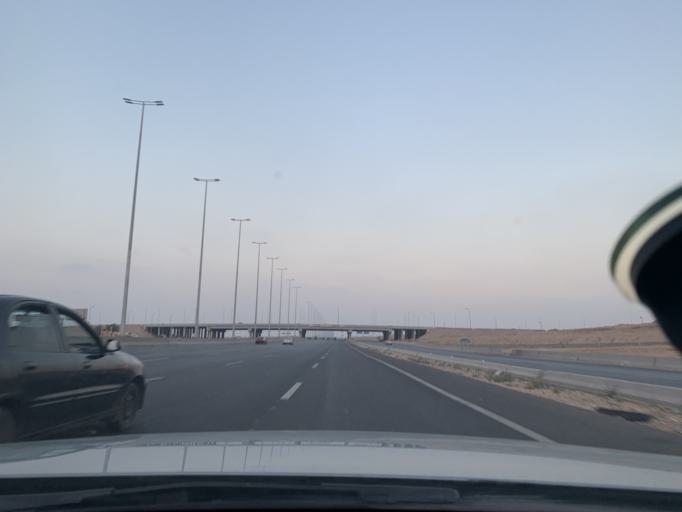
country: EG
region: Muhafazat al Qalyubiyah
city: Al Khankah
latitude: 30.0912
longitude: 31.5025
